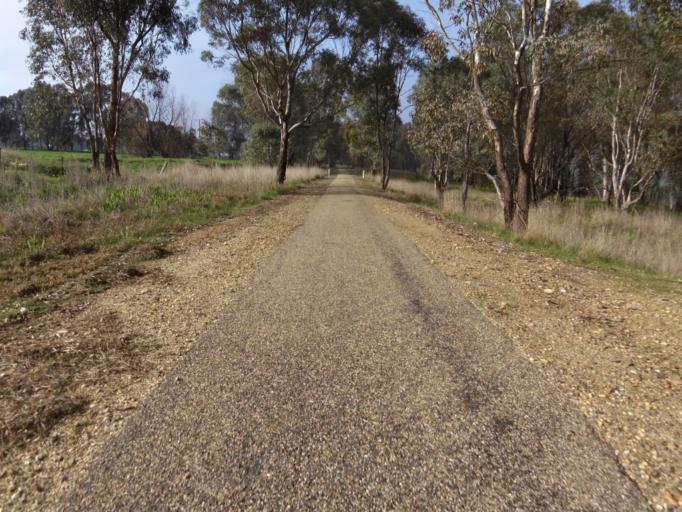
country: AU
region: Victoria
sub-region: Wangaratta
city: Wangaratta
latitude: -36.4499
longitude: 146.5523
